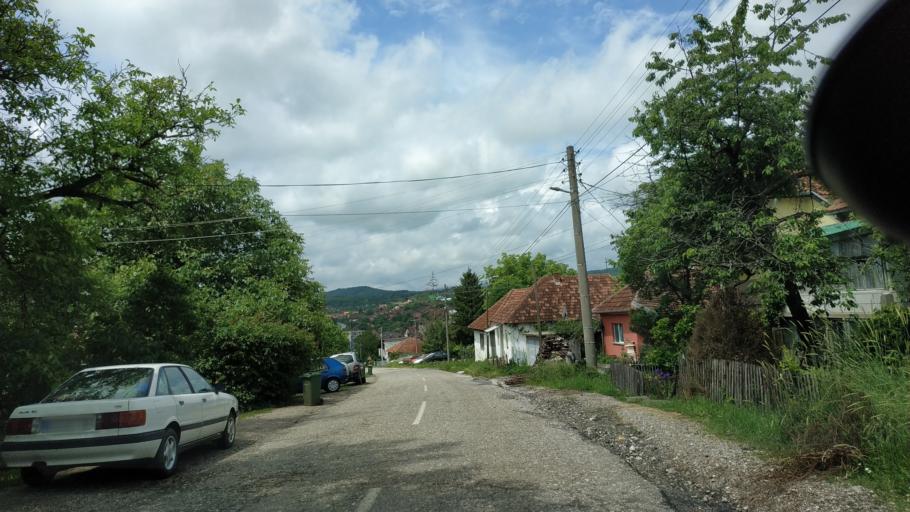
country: RS
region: Central Serbia
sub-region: Zajecarski Okrug
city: Boljevac
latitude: 43.8305
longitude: 21.9662
